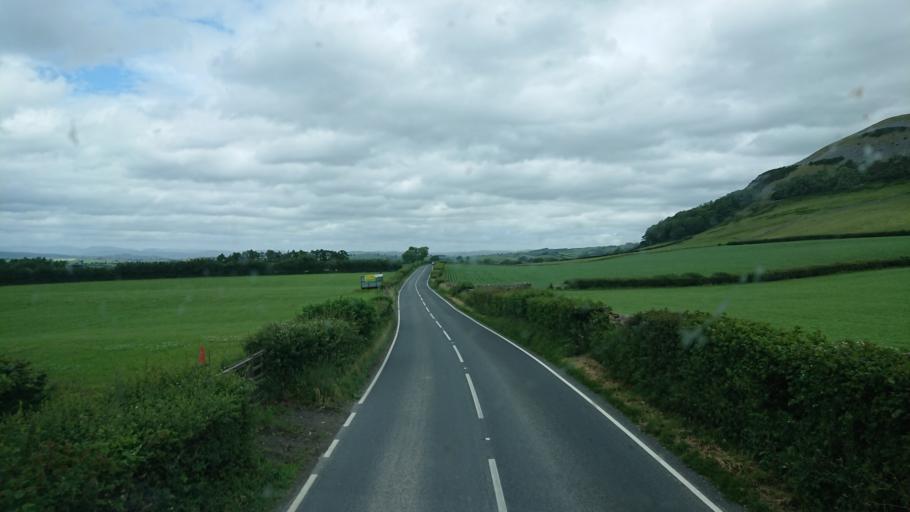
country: GB
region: England
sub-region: Cumbria
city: Milnthorpe
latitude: 54.2130
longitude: -2.7205
